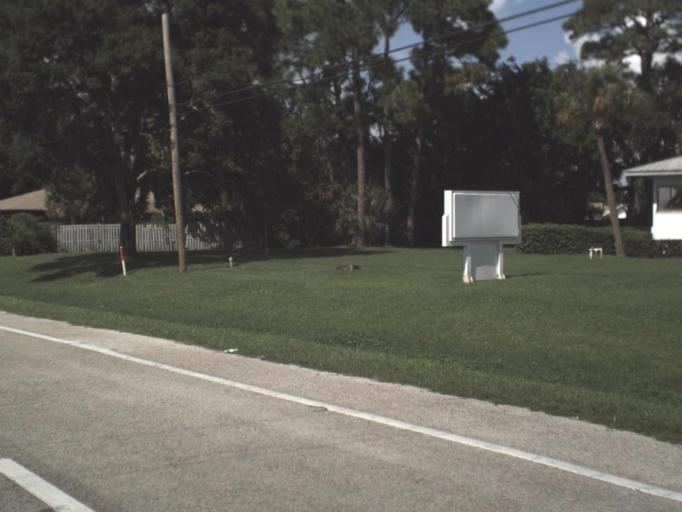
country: US
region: Florida
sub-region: Sarasota County
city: Laurel
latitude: 27.1606
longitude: -82.4725
